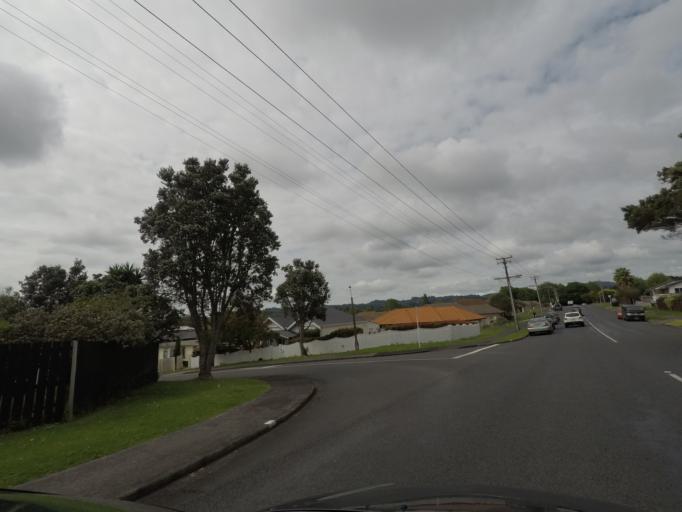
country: NZ
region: Auckland
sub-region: Auckland
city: Waitakere
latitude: -36.9012
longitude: 174.6221
